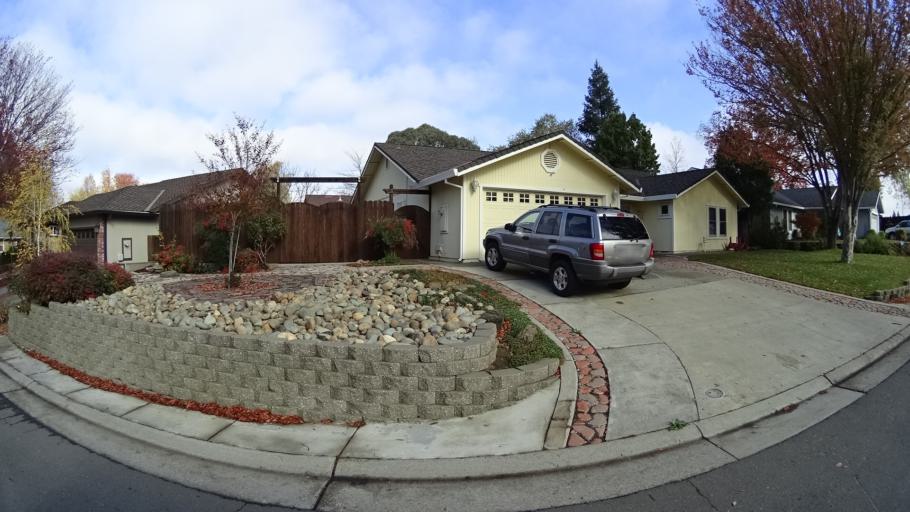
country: US
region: California
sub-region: Sacramento County
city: Antelope
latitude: 38.6905
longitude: -121.3232
